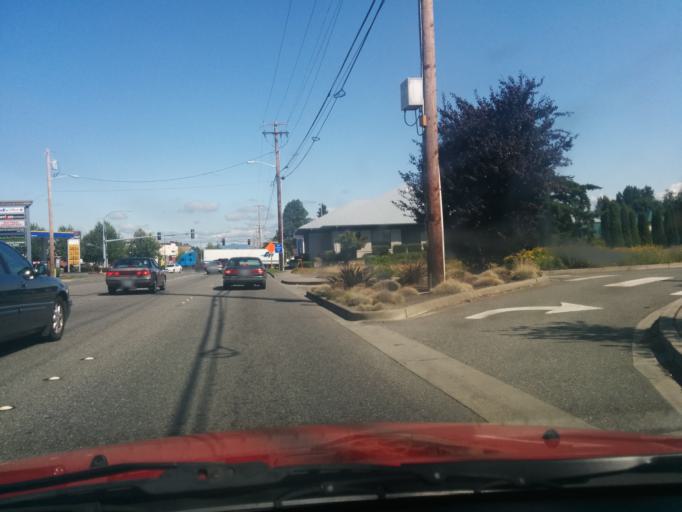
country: US
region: Washington
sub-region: Skagit County
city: Burlington
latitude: 48.4510
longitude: -122.3353
